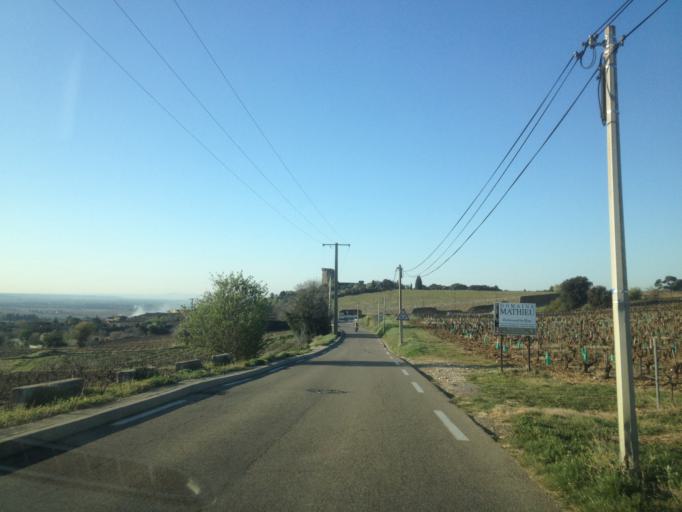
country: FR
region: Provence-Alpes-Cote d'Azur
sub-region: Departement du Vaucluse
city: Chateauneuf-du-Pape
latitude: 44.0636
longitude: 4.8287
